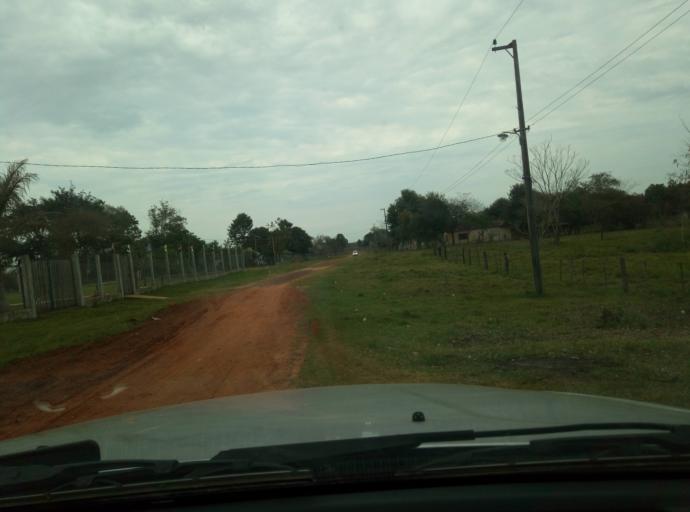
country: PY
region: Caaguazu
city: Carayao
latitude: -25.1540
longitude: -56.3319
